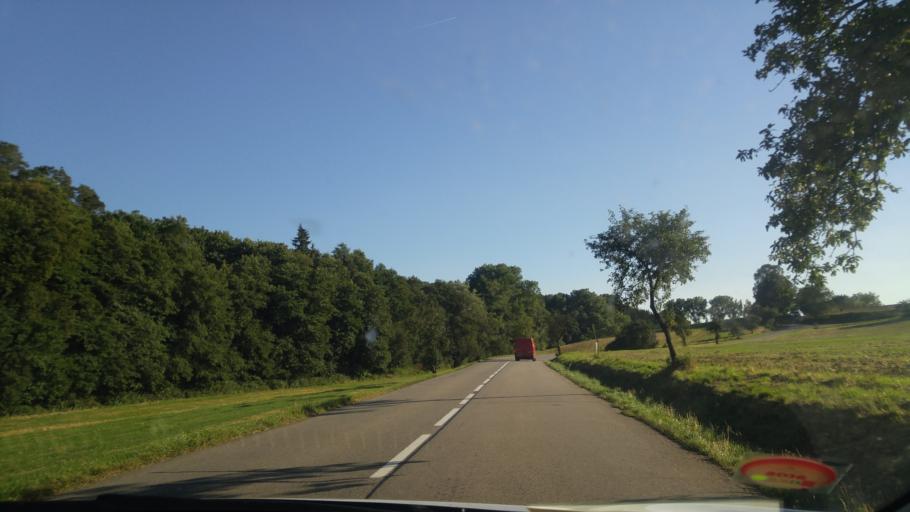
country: CZ
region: South Moravian
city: Veverska Bityska
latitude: 49.2436
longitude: 16.4456
